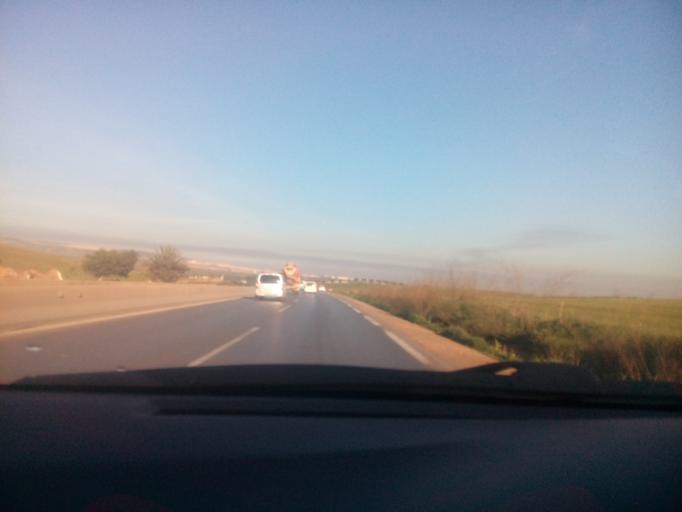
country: DZ
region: Oran
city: Bir el Djir
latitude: 35.7582
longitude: -0.4745
